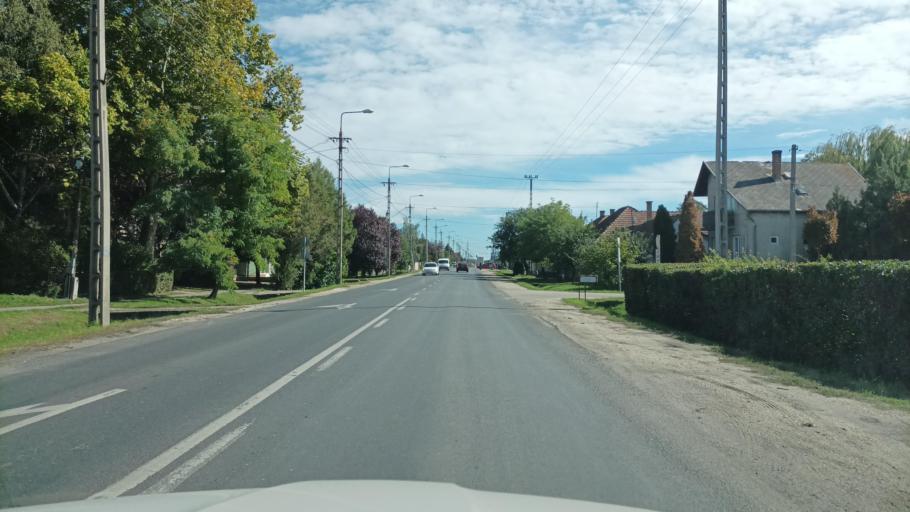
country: HU
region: Pest
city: Ullo
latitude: 47.3829
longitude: 19.3501
